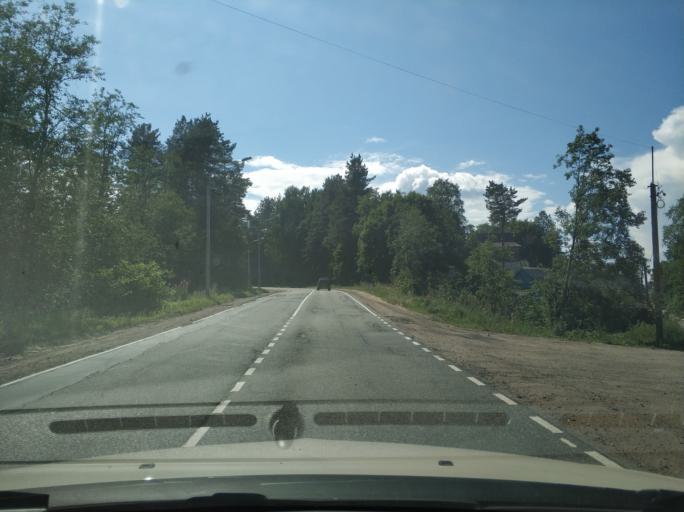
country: RU
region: Leningrad
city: Osel'ki
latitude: 60.2167
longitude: 30.5609
